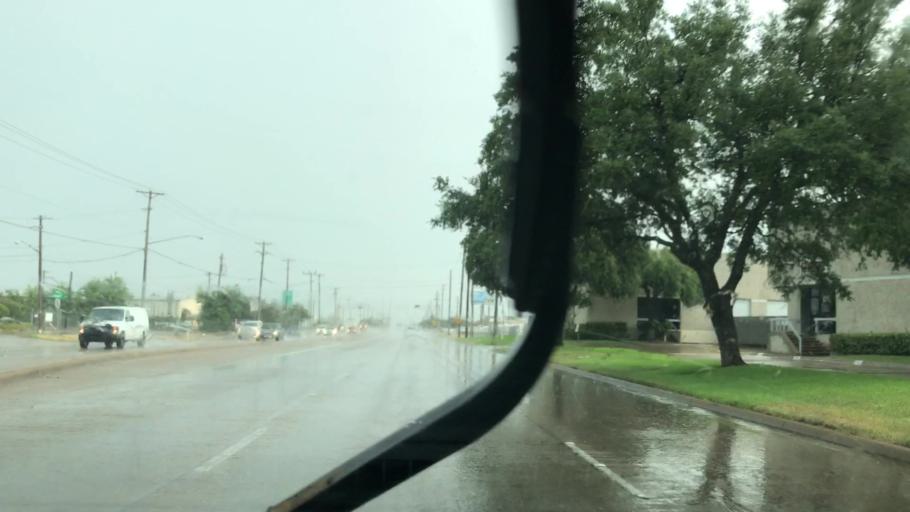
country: US
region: Texas
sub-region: Dallas County
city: Richardson
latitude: 32.9038
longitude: -96.7006
